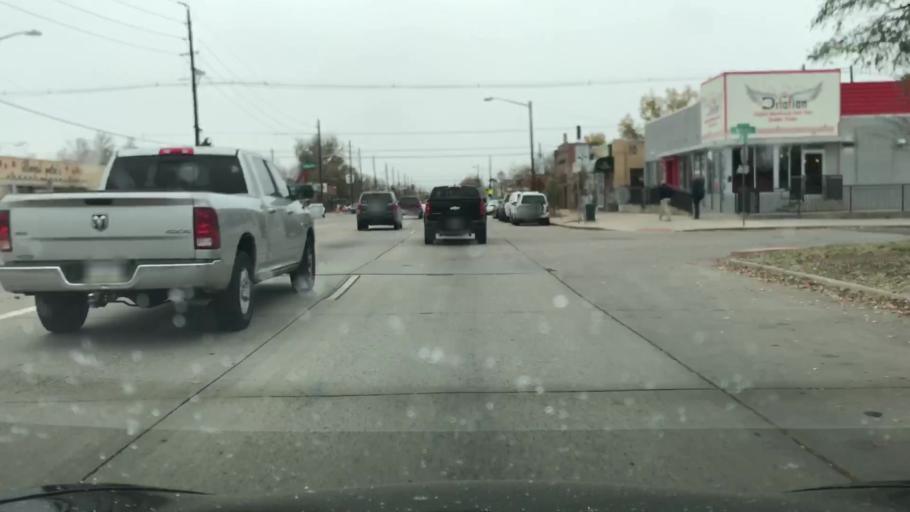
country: US
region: Colorado
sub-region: Arapahoe County
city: Cherry Hills Village
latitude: 39.6785
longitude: -104.9662
